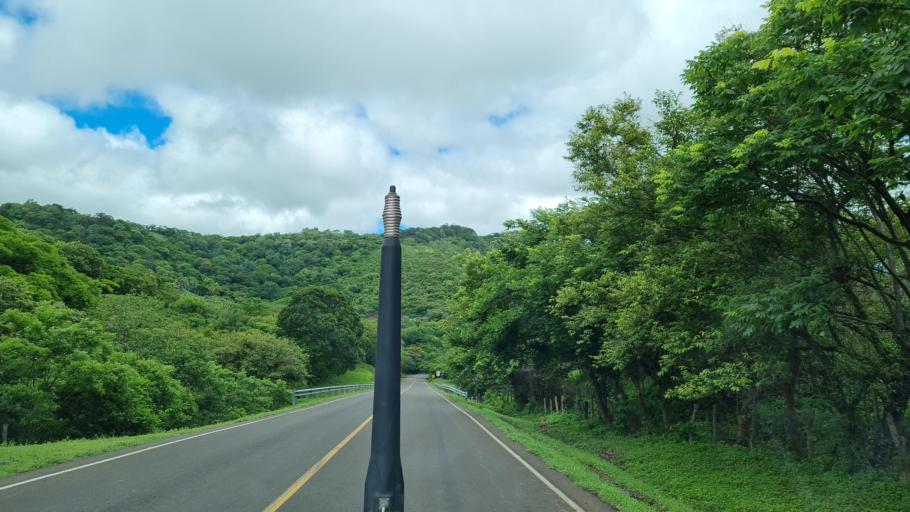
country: NI
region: Matagalpa
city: Terrabona
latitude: 12.5913
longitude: -85.9372
